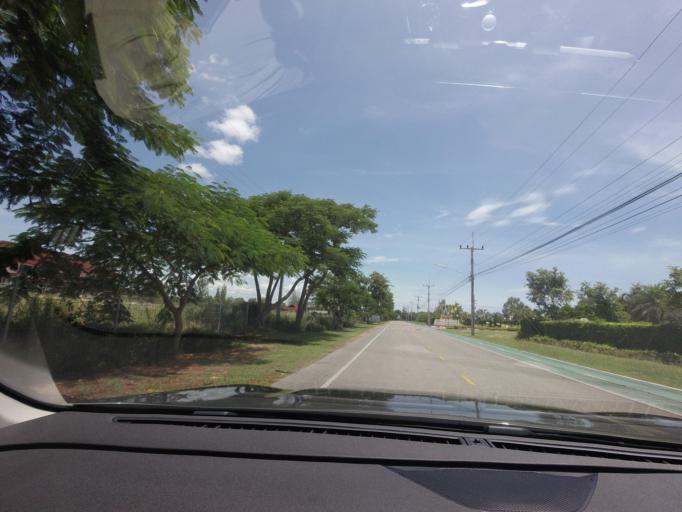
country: TH
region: Prachuap Khiri Khan
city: Hua Hin
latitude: 12.5022
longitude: 99.9727
